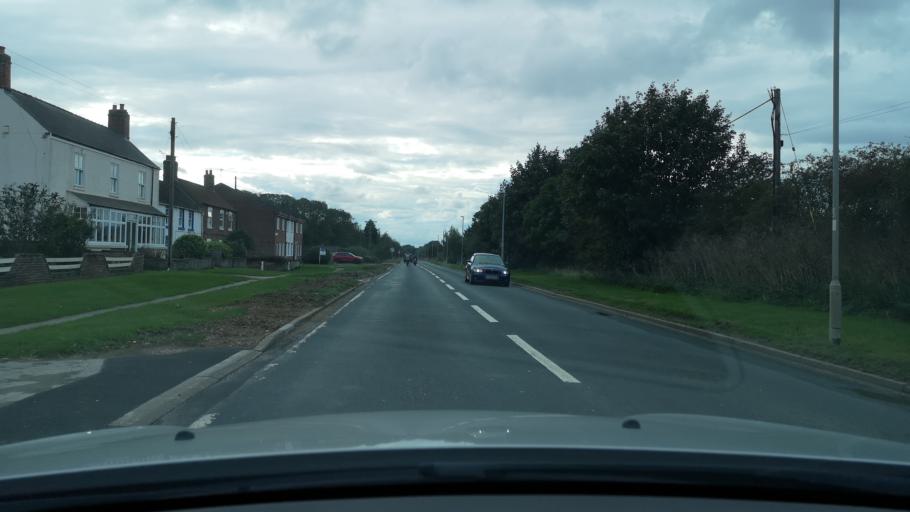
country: GB
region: England
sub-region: East Riding of Yorkshire
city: North Cave
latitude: 53.7773
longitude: -0.6585
